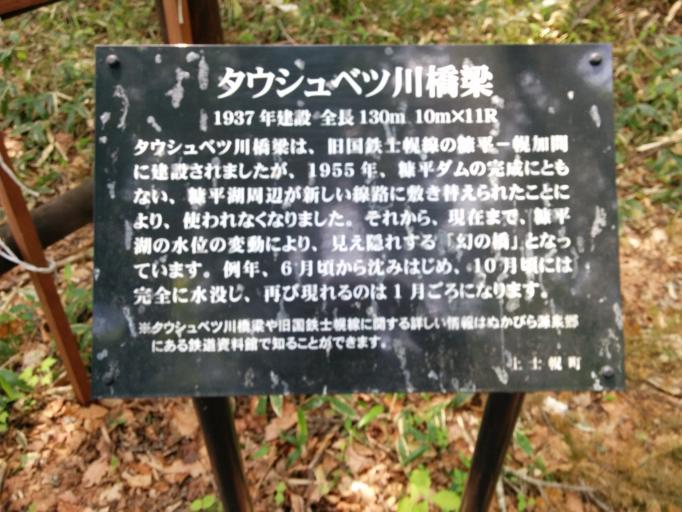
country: JP
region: Hokkaido
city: Otofuke
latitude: 43.4143
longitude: 143.1797
